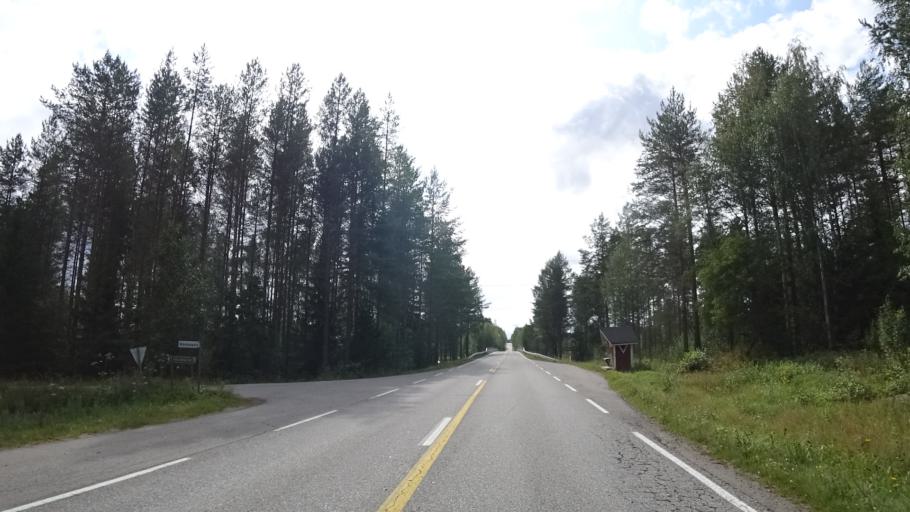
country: FI
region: North Karelia
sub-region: Joensuu
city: Ilomantsi
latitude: 62.7594
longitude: 31.0140
